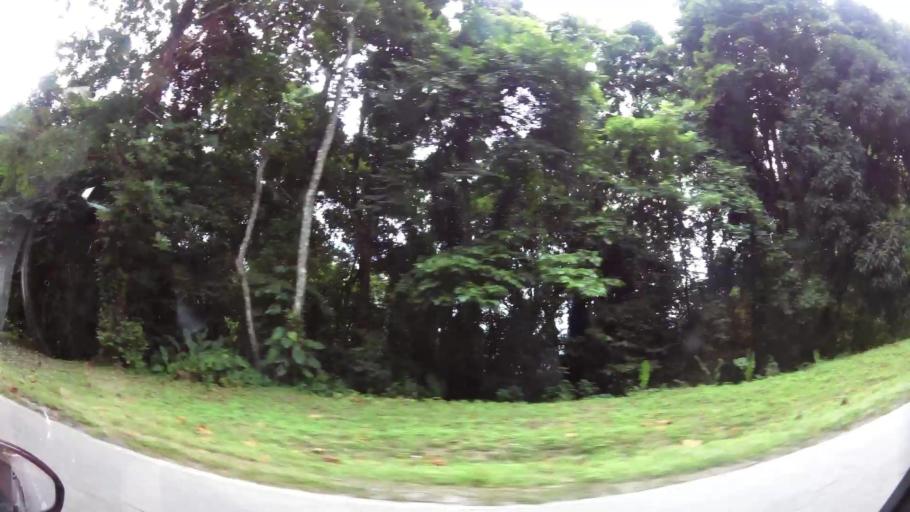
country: TT
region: Diego Martin
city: Petit Valley
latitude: 10.7470
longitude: -61.4852
